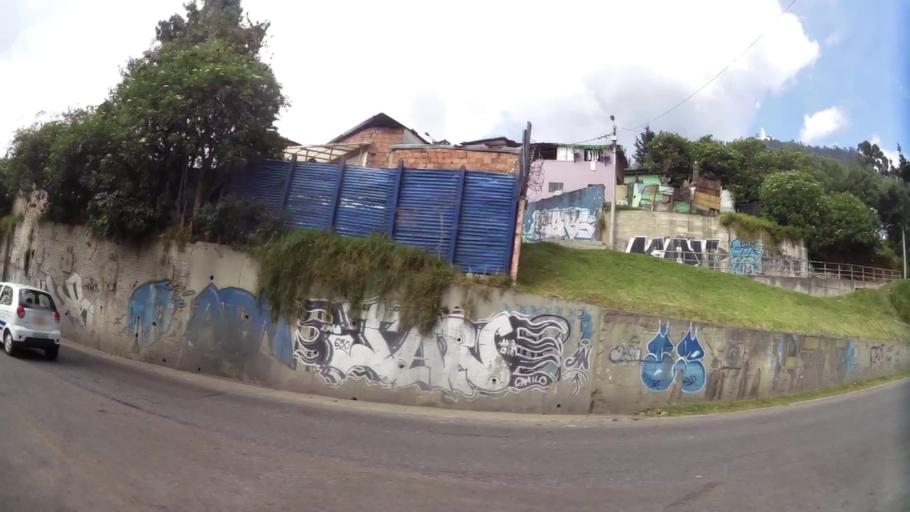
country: CO
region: Bogota D.C.
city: Bogota
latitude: 4.6060
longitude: -74.0653
